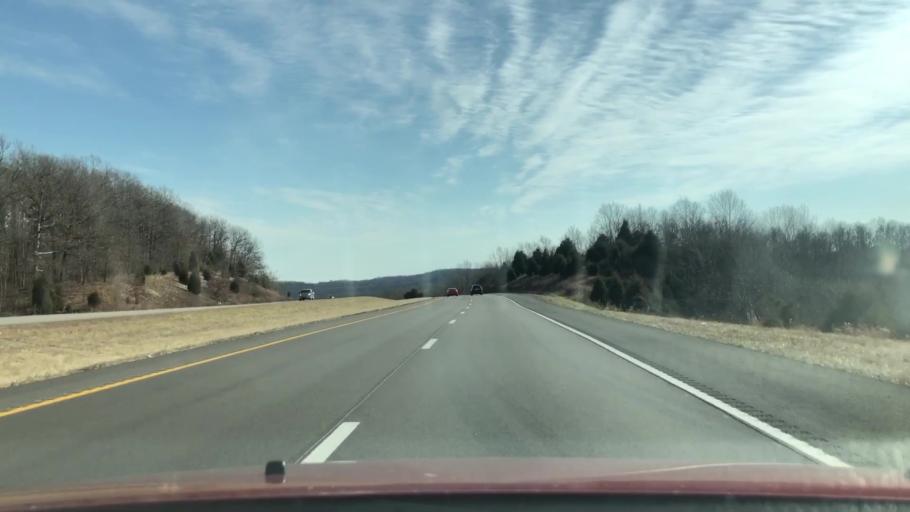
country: US
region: Missouri
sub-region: Wright County
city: Mansfield
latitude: 37.1141
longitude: -92.6722
